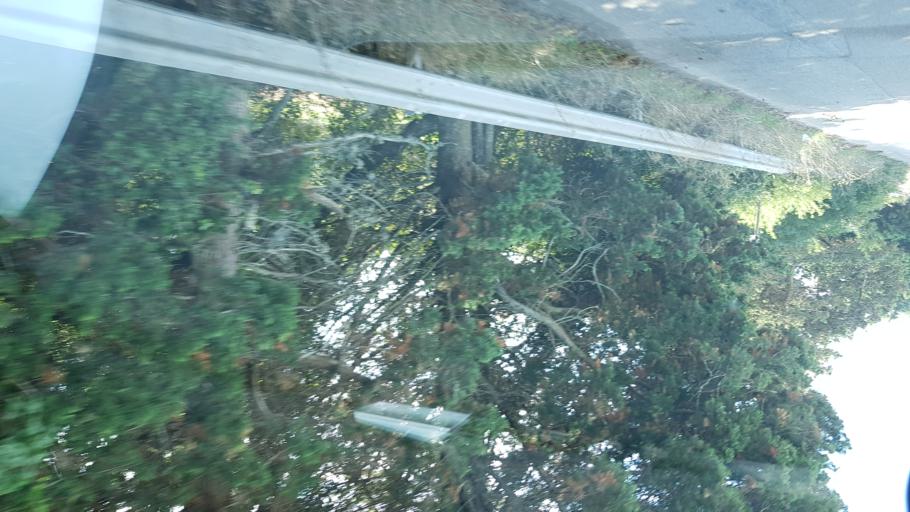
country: IT
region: Apulia
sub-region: Provincia di Lecce
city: Borgagne
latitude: 40.2228
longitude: 18.4411
